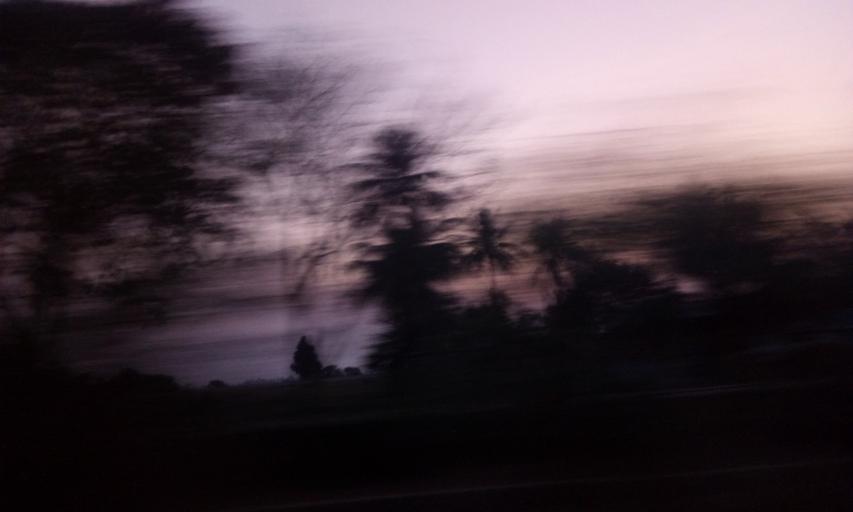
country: TH
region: Sing Buri
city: Sing Buri
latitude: 14.8353
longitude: 100.3977
